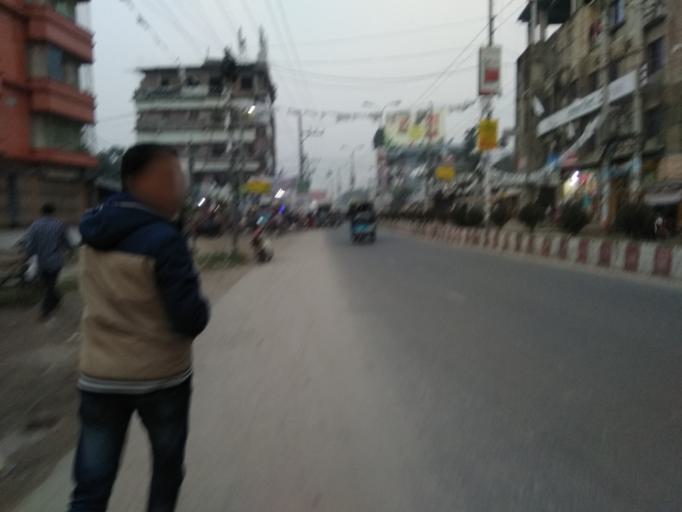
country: BD
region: Rangpur Division
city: Rangpur
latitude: 25.7323
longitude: 89.2547
